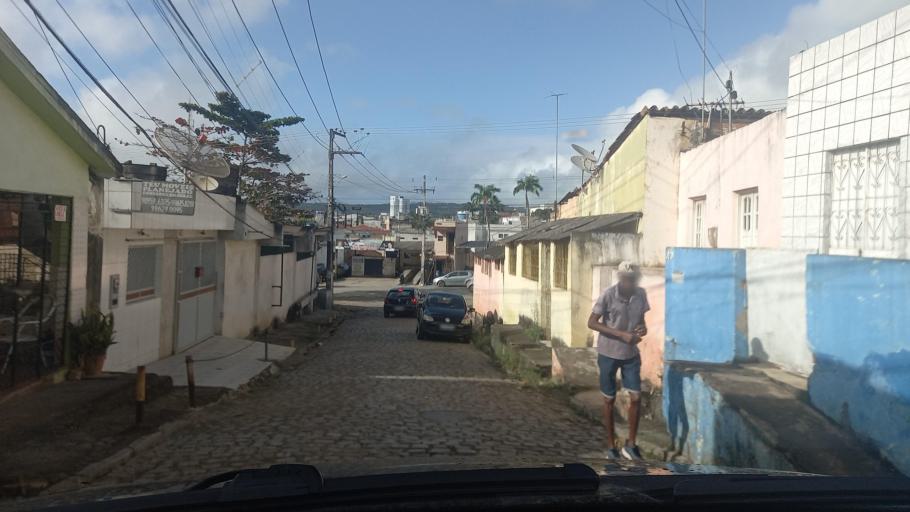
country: BR
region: Pernambuco
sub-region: Vitoria De Santo Antao
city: Vitoria de Santo Antao
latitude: -8.1170
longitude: -35.3062
